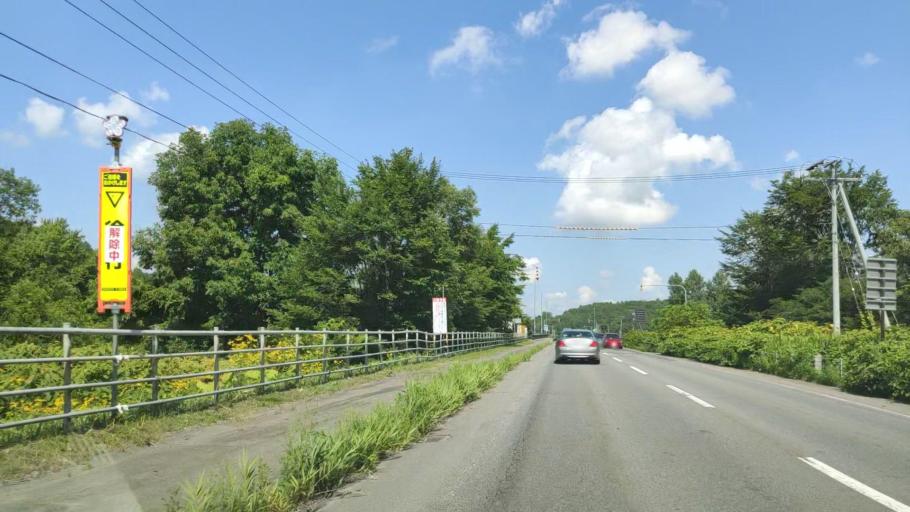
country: JP
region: Hokkaido
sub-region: Asahikawa-shi
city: Asahikawa
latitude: 43.6238
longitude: 142.4676
